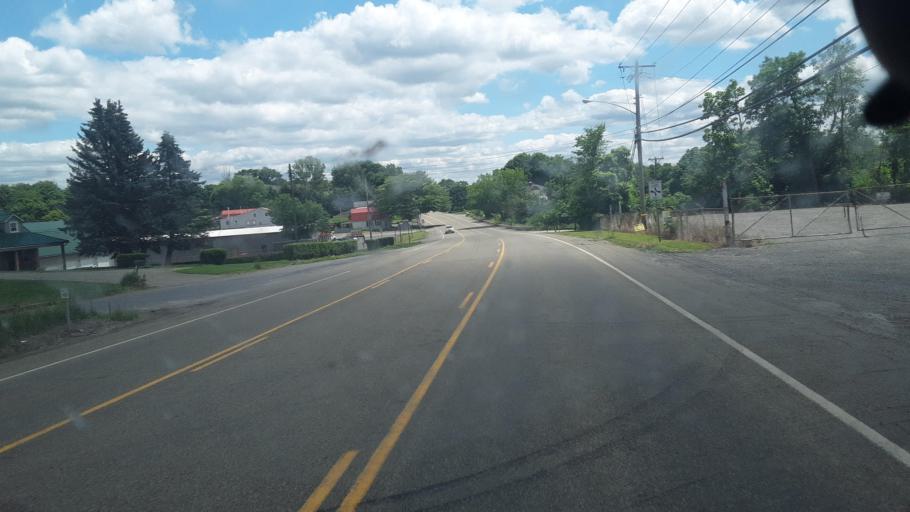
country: US
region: Pennsylvania
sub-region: Butler County
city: Prospect
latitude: 40.9297
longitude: -80.1457
